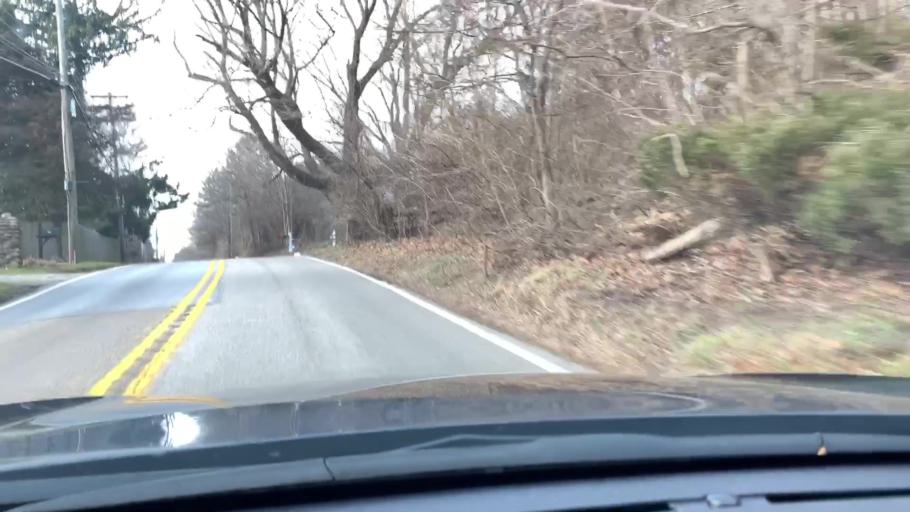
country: US
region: Pennsylvania
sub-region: Delaware County
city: Broomall
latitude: 39.9980
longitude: -75.3968
